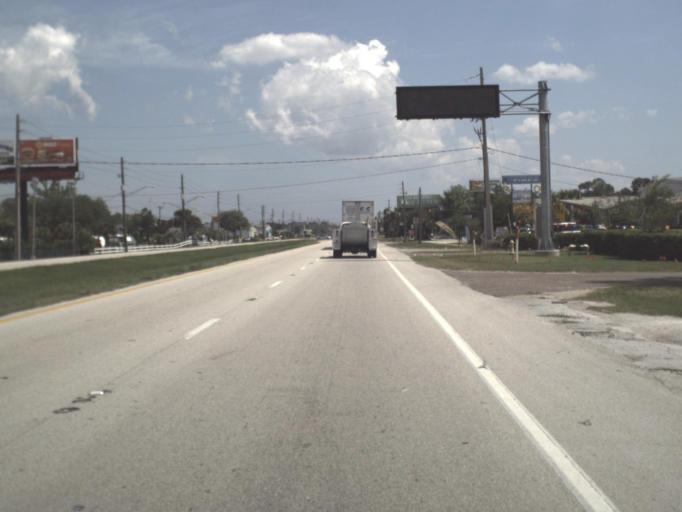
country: US
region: Florida
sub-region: Duval County
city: Jacksonville
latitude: 30.2728
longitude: -81.6232
